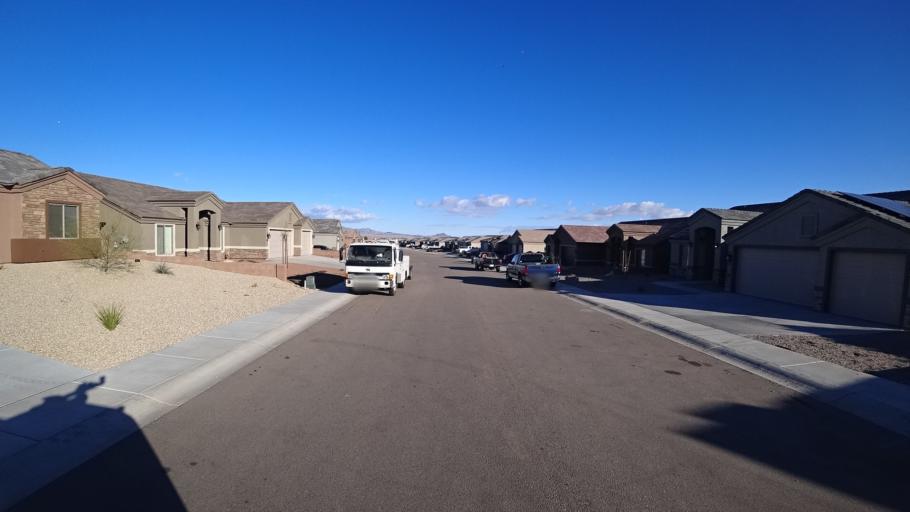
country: US
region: Arizona
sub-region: Mohave County
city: New Kingman-Butler
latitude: 35.2187
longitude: -113.9696
